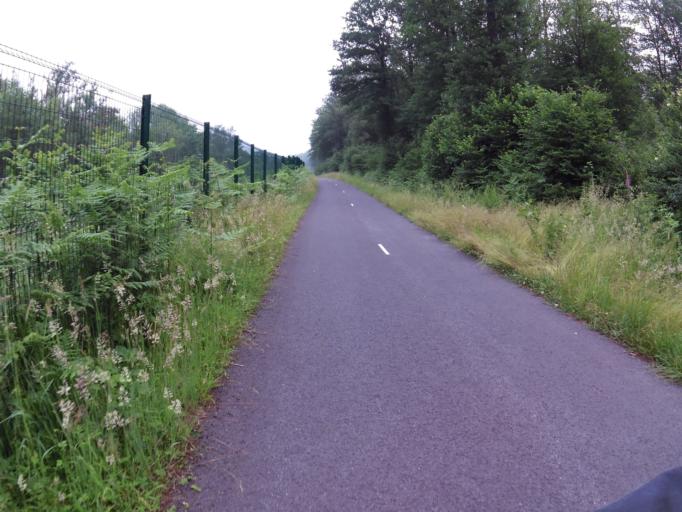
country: FR
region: Champagne-Ardenne
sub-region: Departement des Ardennes
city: Revin
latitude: 49.9605
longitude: 4.6599
